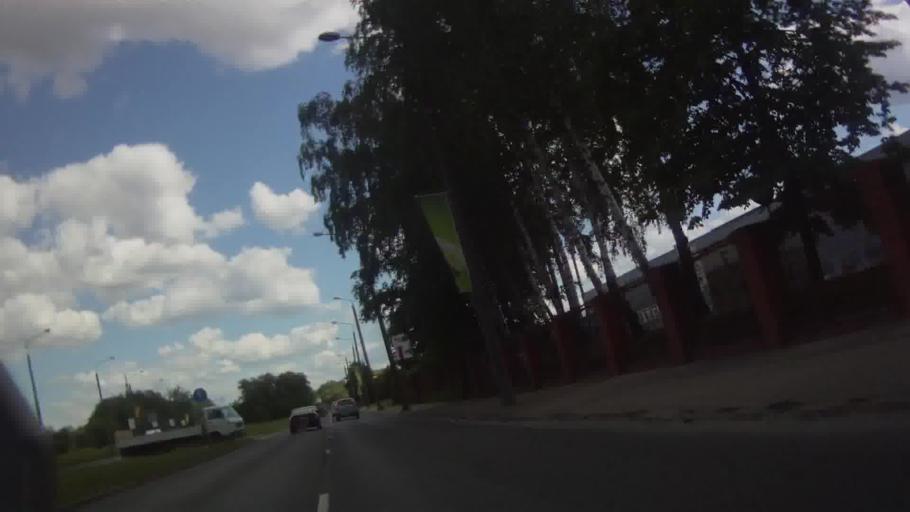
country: LV
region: Riga
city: Riga
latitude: 56.9187
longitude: 24.1142
